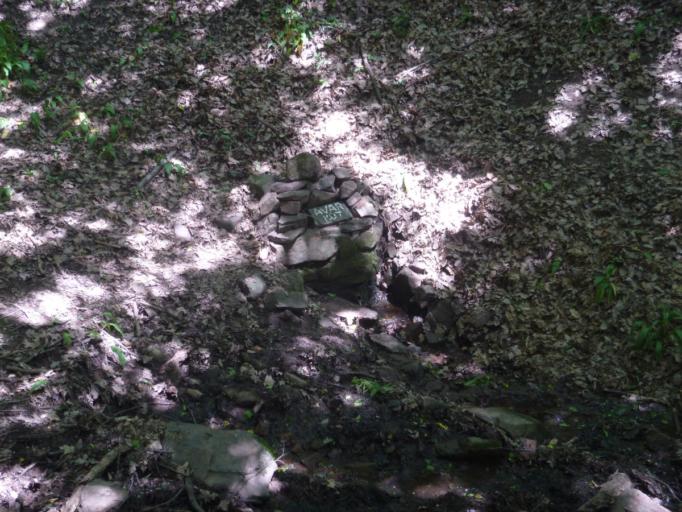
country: HU
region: Baranya
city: Pellerd
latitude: 46.0895
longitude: 18.1616
